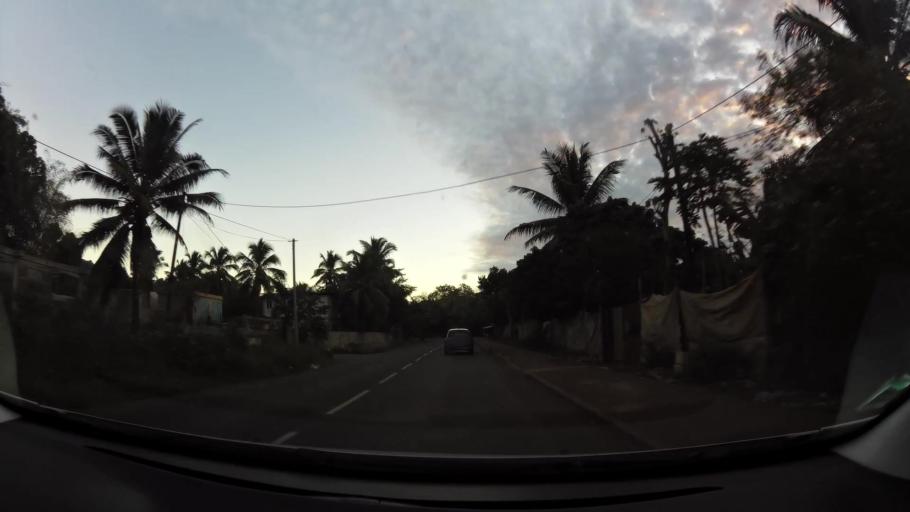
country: YT
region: Koungou
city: Koungou
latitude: -12.7342
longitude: 45.1594
